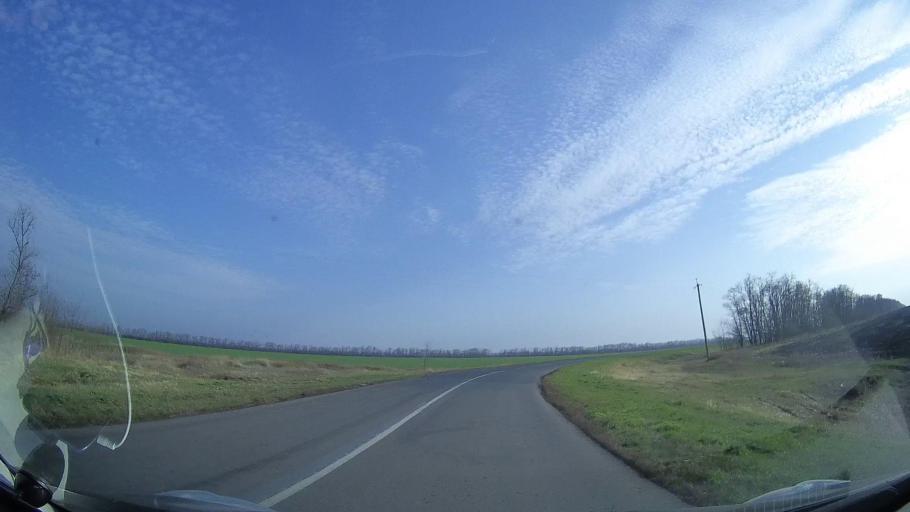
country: RU
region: Rostov
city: Mechetinskaya
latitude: 46.9038
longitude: 40.5404
